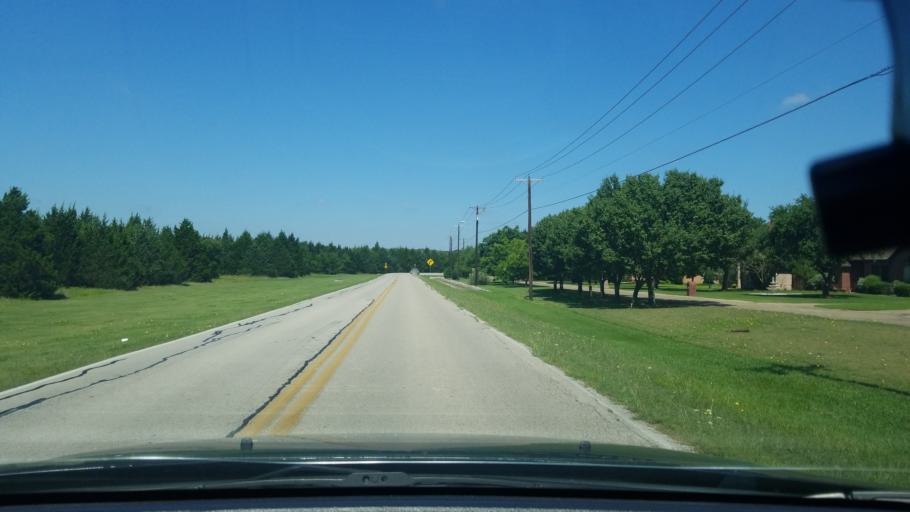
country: US
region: Texas
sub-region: Dallas County
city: Sunnyvale
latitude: 32.7962
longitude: -96.5904
